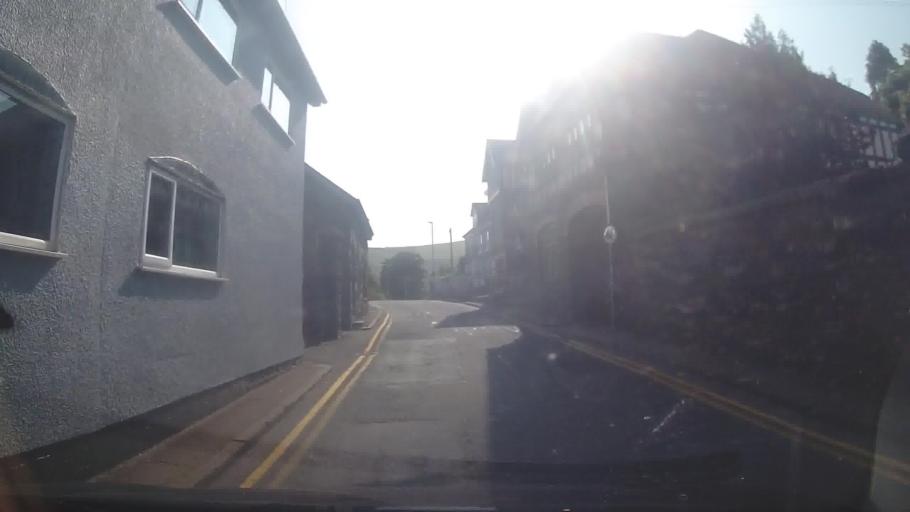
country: GB
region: Wales
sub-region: Sir Powys
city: Rhayader
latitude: 52.2998
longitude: -3.5098
